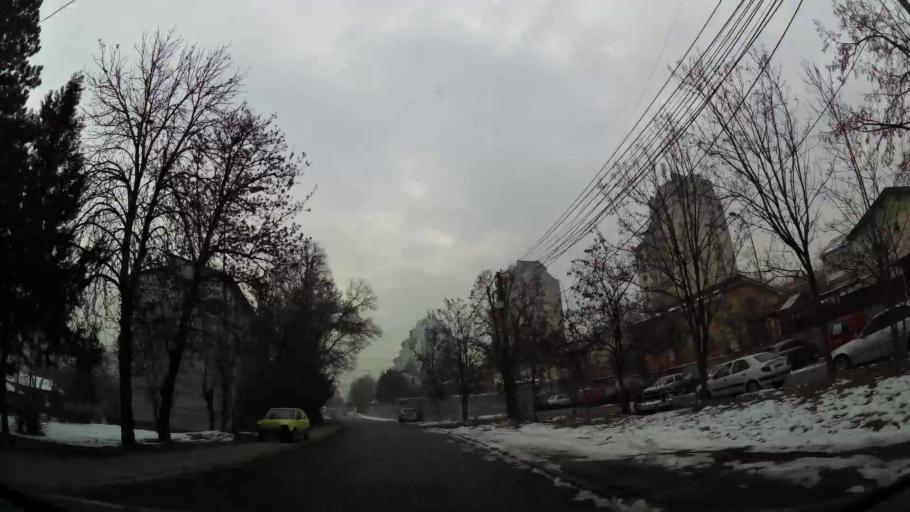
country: MK
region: Cair
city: Cair
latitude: 42.0122
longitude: 21.4603
